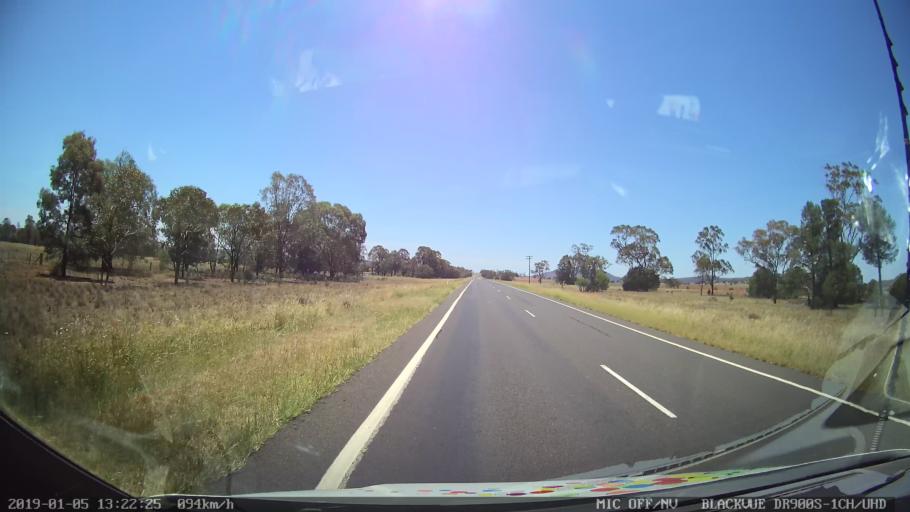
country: AU
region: New South Wales
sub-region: Gunnedah
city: Gunnedah
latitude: -31.0864
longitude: 149.9616
